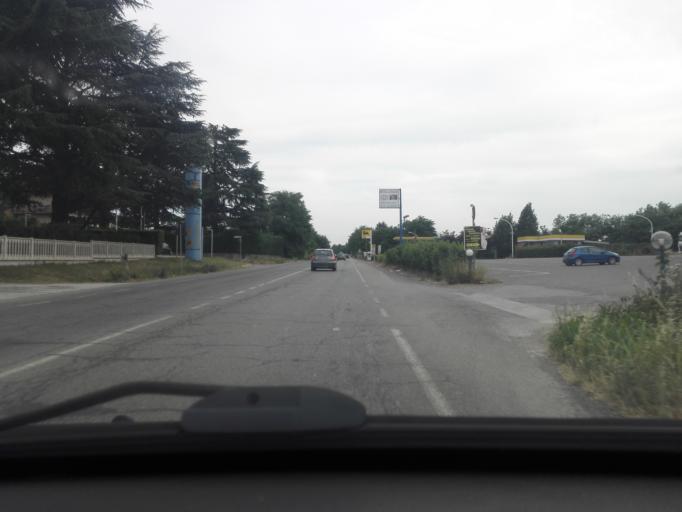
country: IT
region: Piedmont
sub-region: Provincia di Alessandria
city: Pozzolo Formigaro
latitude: 44.7965
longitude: 8.7781
